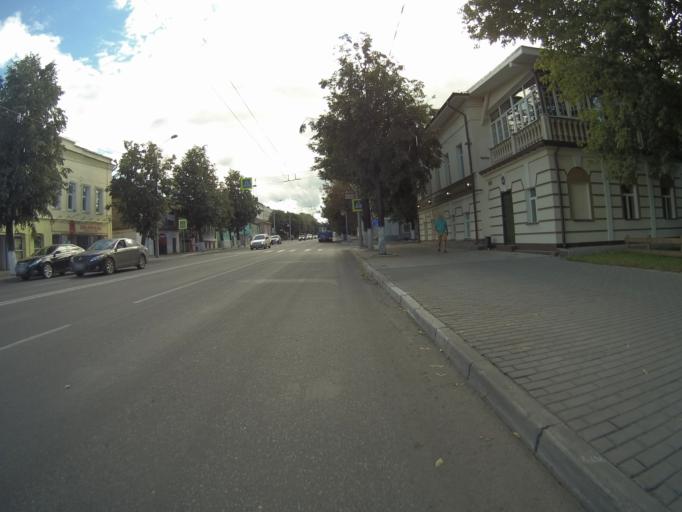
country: RU
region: Vladimir
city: Vladimir
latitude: 56.1351
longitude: 40.4239
